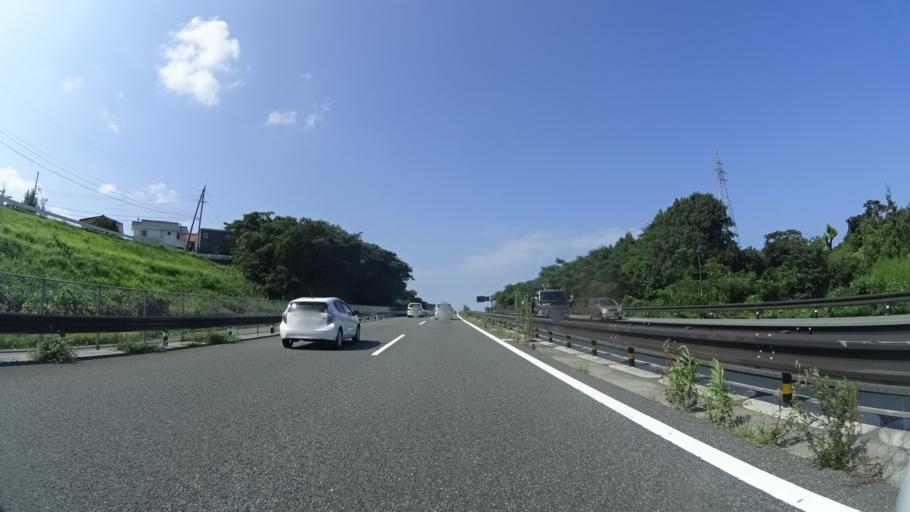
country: JP
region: Shimane
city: Hamada
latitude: 34.8923
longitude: 132.0792
